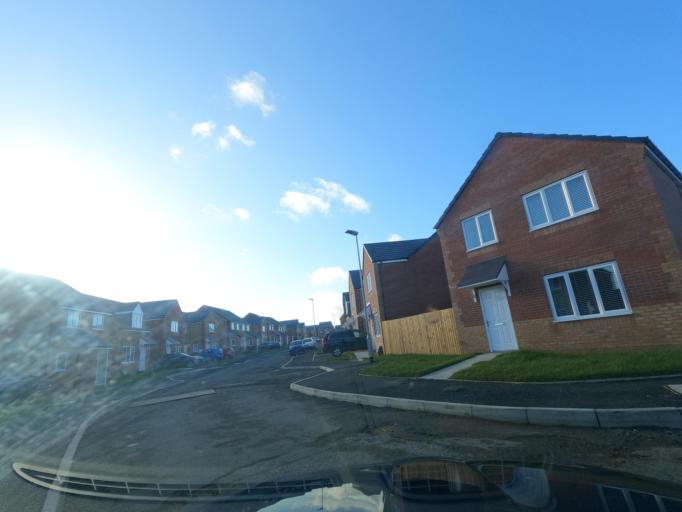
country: GB
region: England
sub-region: Northumberland
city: Lynemouth
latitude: 55.1830
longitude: -1.5468
